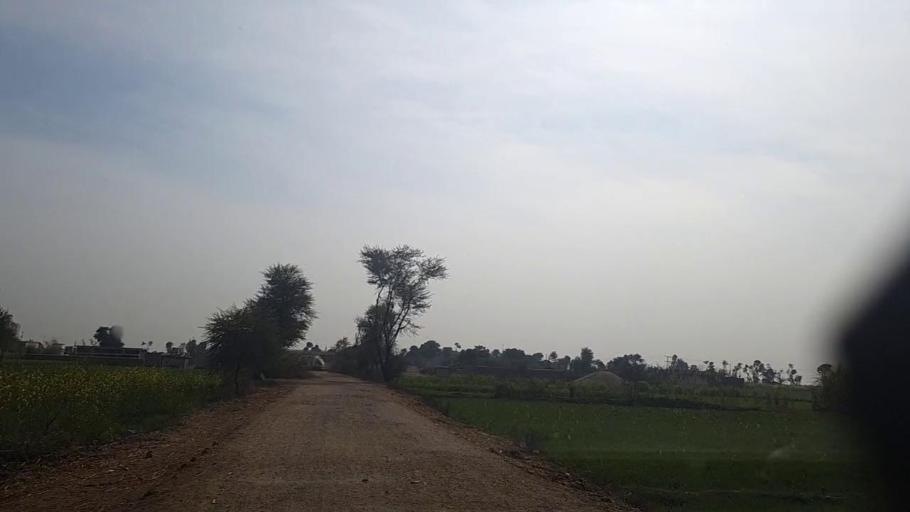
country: PK
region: Sindh
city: Daur
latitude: 26.4041
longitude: 68.2390
